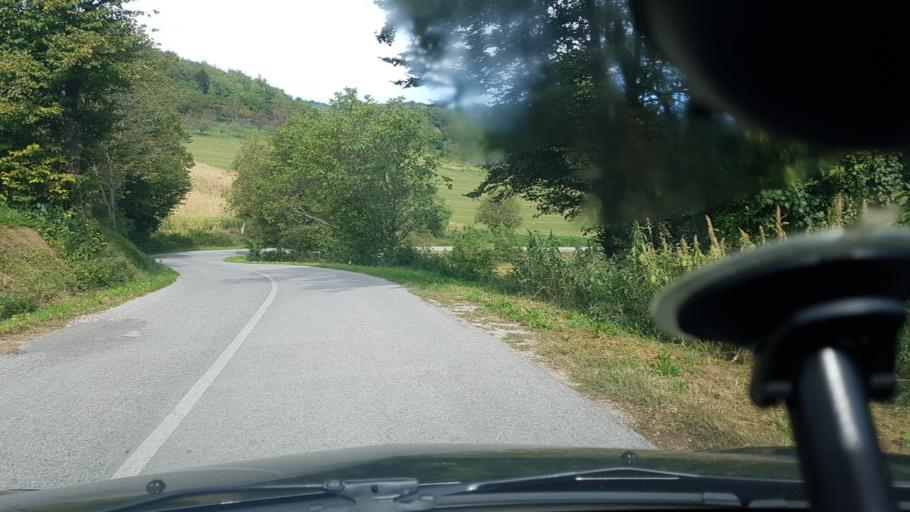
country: HR
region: Varazdinska
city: Ljubescica
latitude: 46.0958
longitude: 16.3402
